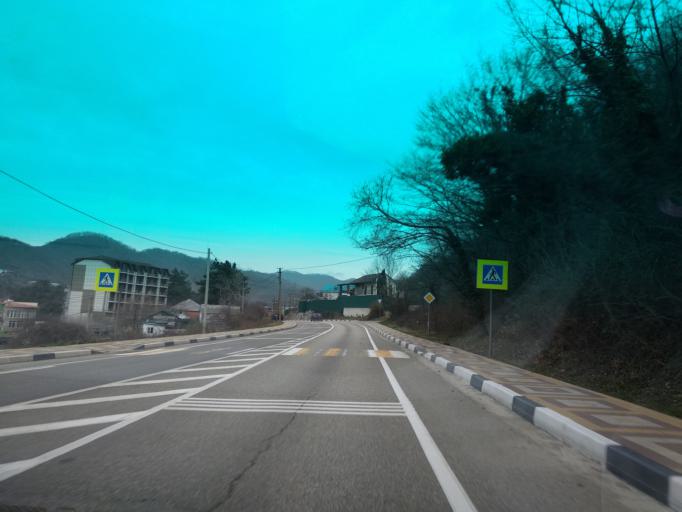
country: RU
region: Krasnodarskiy
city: Ol'ginka
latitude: 44.1955
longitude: 38.8918
